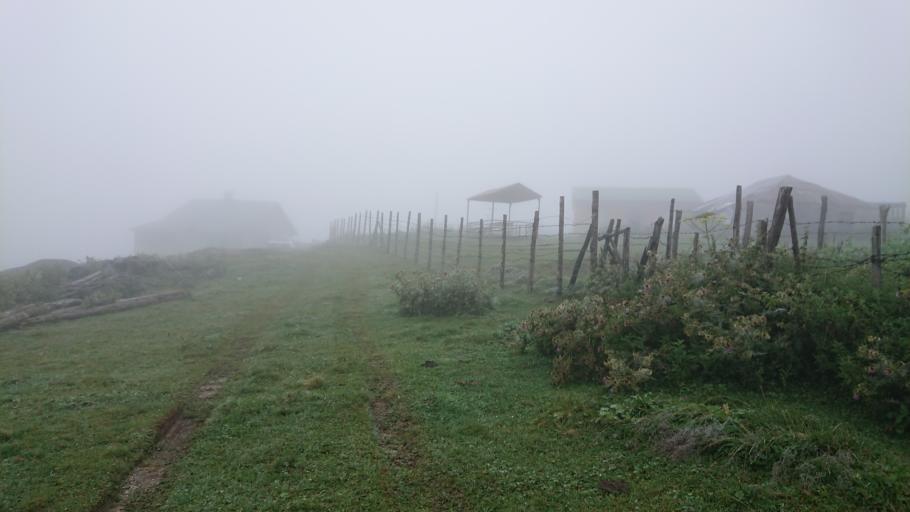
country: TR
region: Gumushane
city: Kurtun
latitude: 40.6729
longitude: 38.9936
